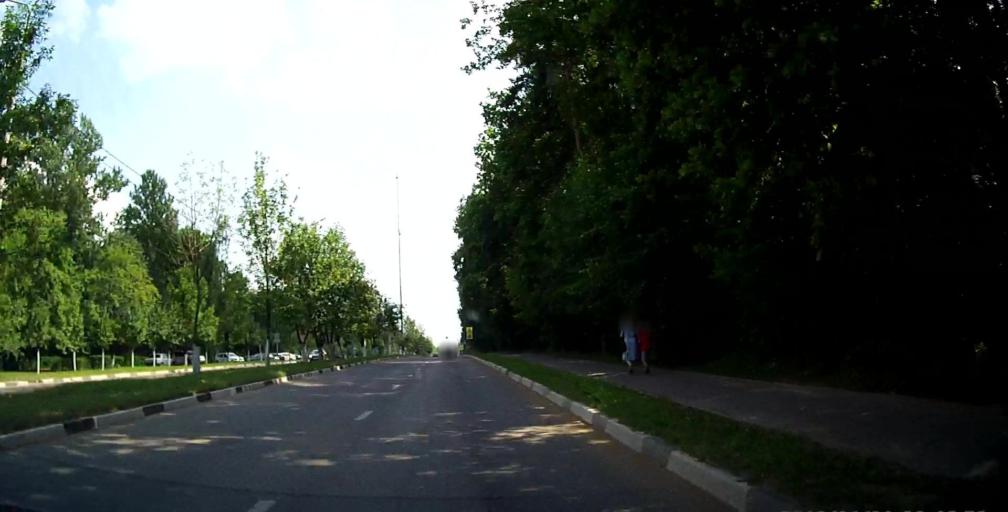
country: RU
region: Moskovskaya
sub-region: Podol'skiy Rayon
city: Podol'sk
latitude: 55.4170
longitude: 37.5206
